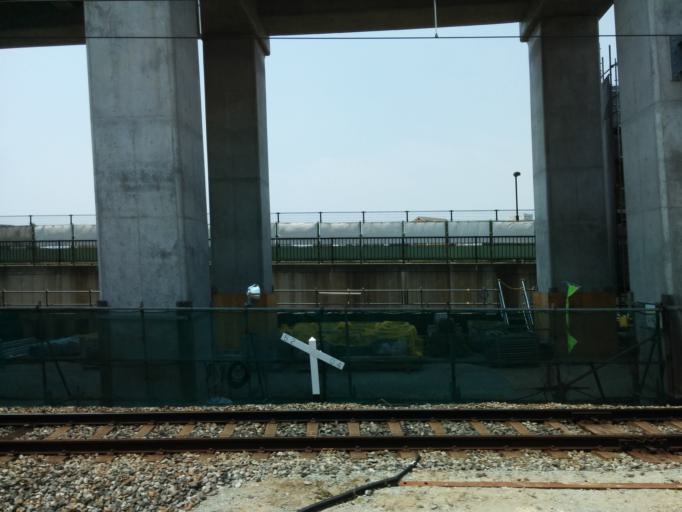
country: JP
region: Osaka
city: Suita
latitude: 34.7362
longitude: 135.5161
